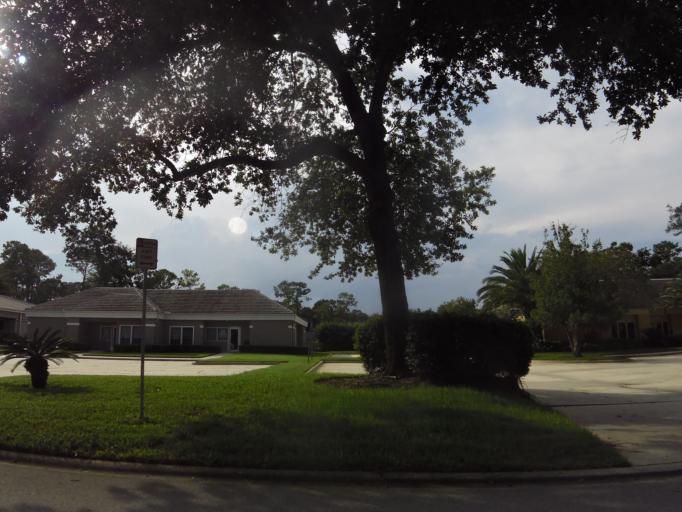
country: US
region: Florida
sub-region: Clay County
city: Orange Park
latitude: 30.2072
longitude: -81.6188
